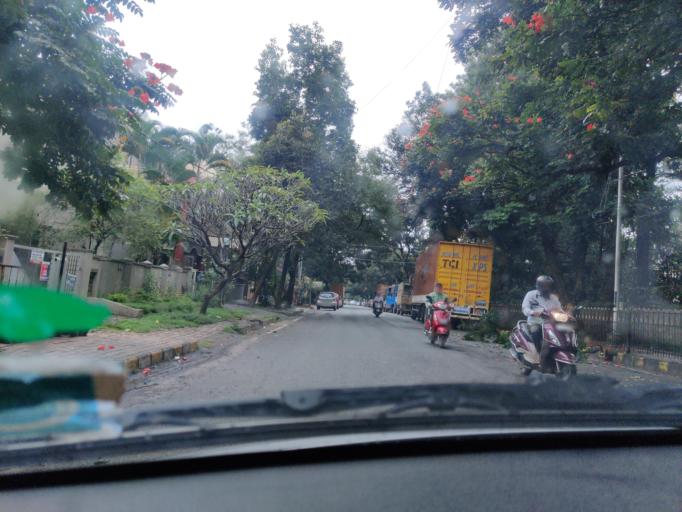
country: IN
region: Karnataka
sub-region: Bangalore Urban
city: Bangalore
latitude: 13.0205
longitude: 77.6395
